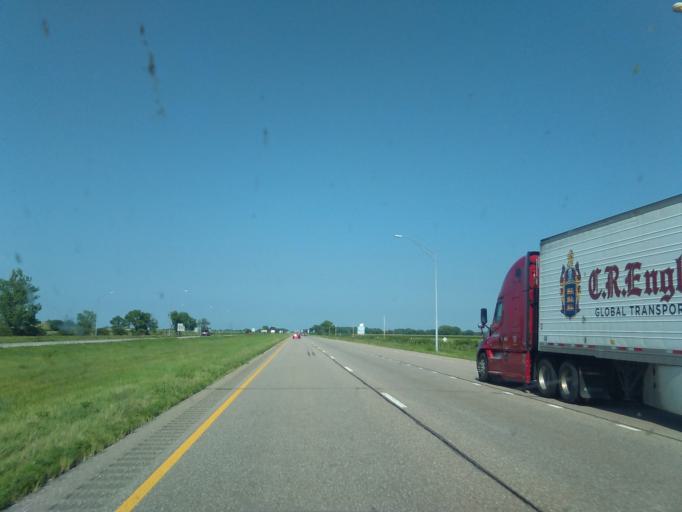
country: US
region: Nebraska
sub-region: Hall County
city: Wood River
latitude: 40.7995
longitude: -98.4899
